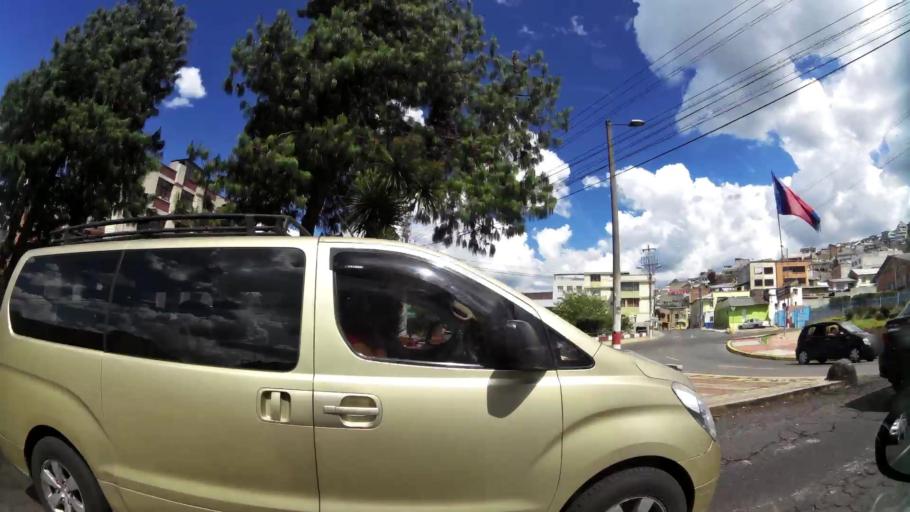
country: EC
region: Pichincha
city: Quito
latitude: -0.2060
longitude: -78.5091
